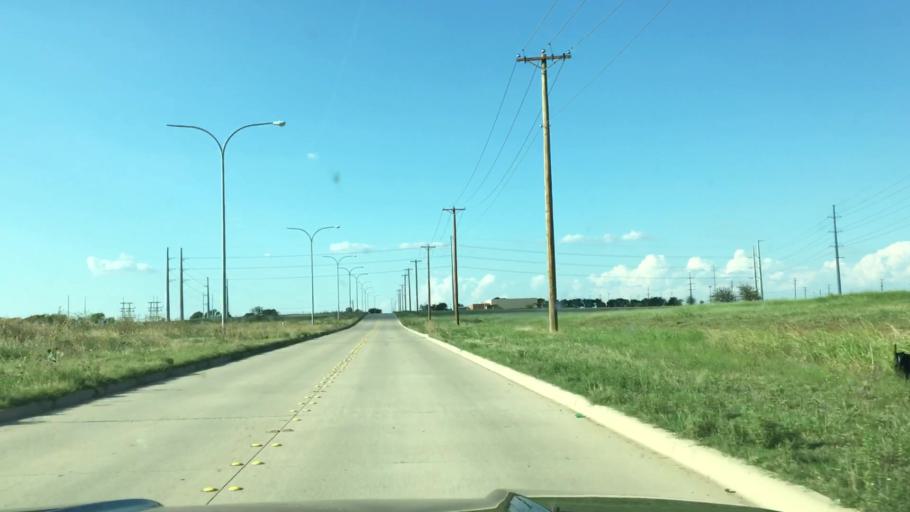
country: US
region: Texas
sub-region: Tarrant County
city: Haslet
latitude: 32.9944
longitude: -97.3589
